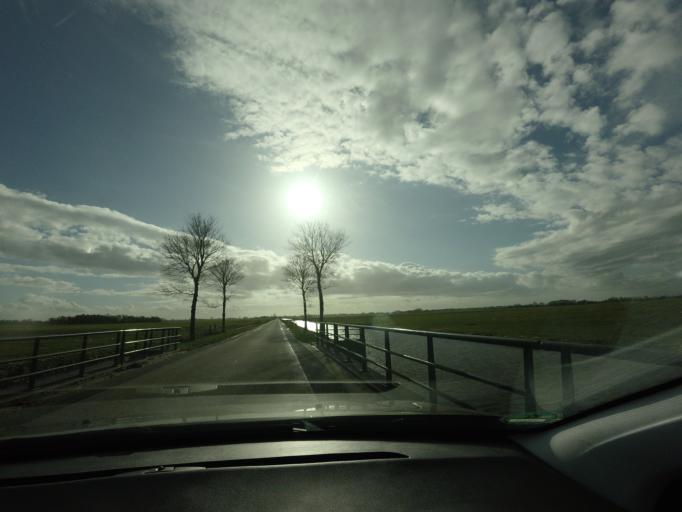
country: NL
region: Friesland
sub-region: Sudwest Fryslan
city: Scharnegoutum
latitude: 53.0513
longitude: 5.7276
